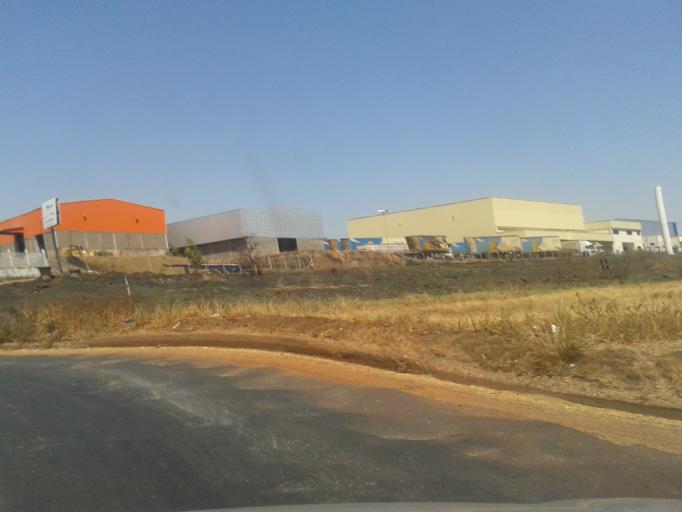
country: BR
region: Minas Gerais
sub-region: Uberlandia
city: Uberlandia
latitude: -18.8613
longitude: -48.2953
